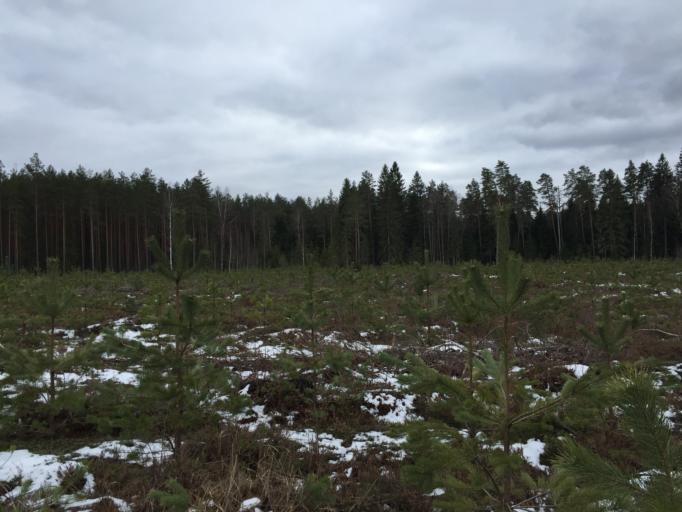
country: LV
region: Garkalne
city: Garkalne
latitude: 56.9648
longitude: 24.4756
